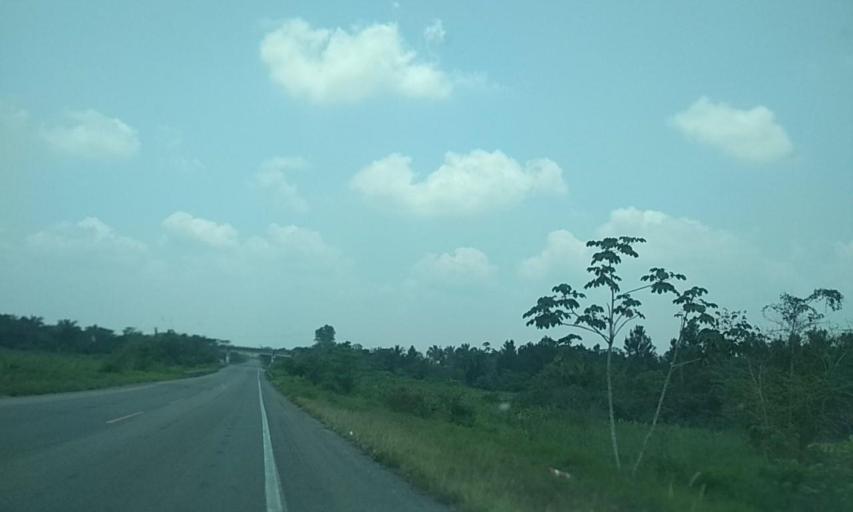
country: MX
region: Tabasco
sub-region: Huimanguillo
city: Francisco Rueda
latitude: 17.7553
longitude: -94.0015
